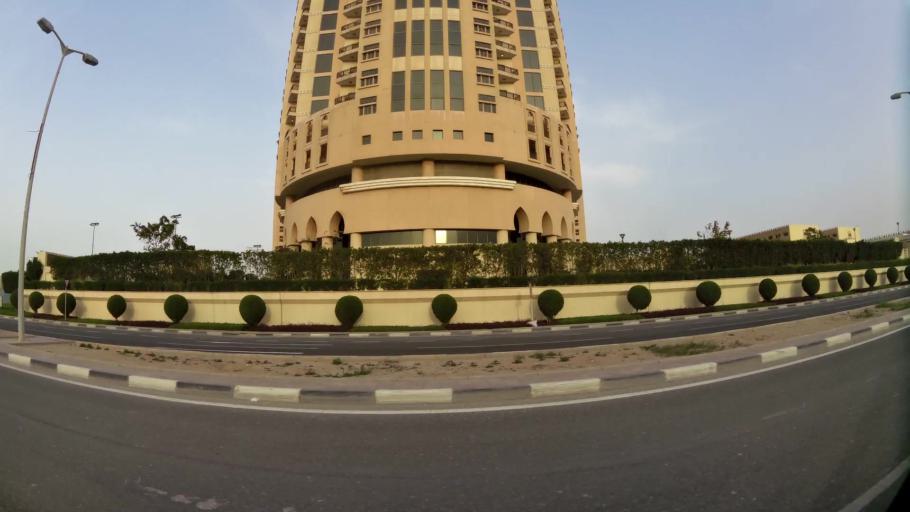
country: QA
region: Baladiyat ad Dawhah
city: Doha
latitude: 25.3503
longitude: 51.5262
